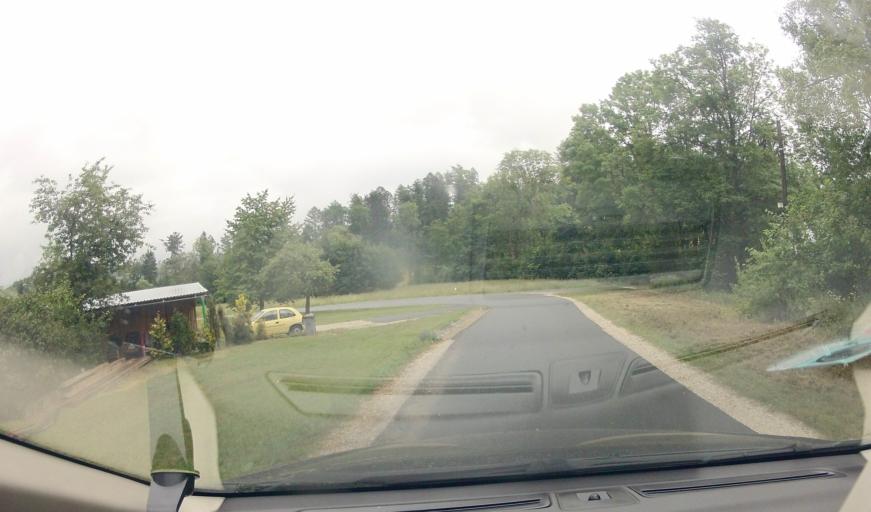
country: PL
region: Lower Silesian Voivodeship
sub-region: Powiat klodzki
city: Miedzylesie
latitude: 50.1211
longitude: 16.6588
